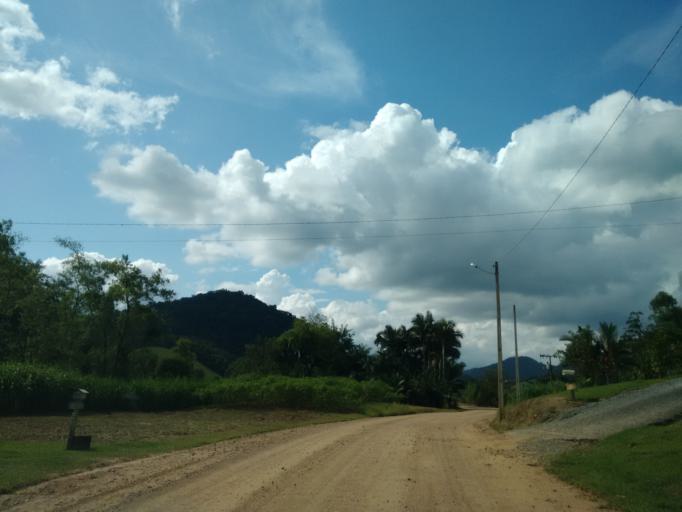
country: BR
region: Santa Catarina
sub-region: Pomerode
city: Pomerode
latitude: -26.8154
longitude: -49.1430
